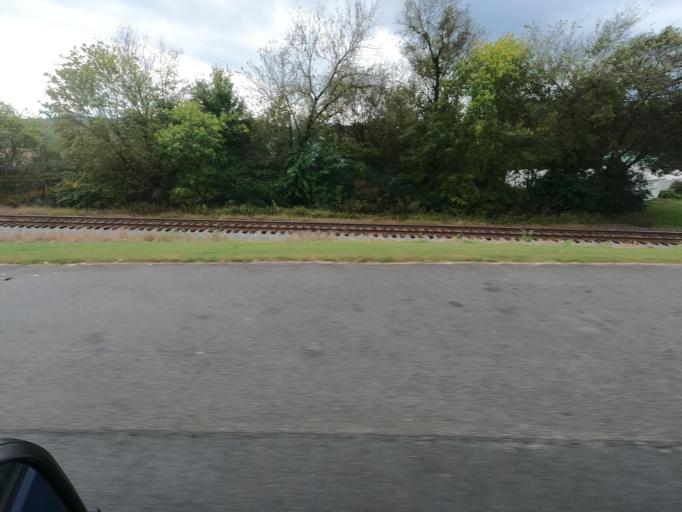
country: US
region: Tennessee
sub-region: Cheatham County
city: Pegram
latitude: 36.0995
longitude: -87.0496
